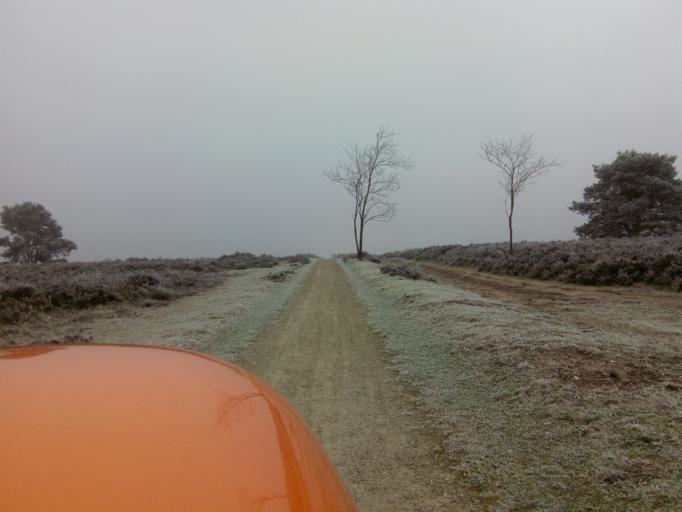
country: NL
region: Gelderland
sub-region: Gemeente Barneveld
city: Garderen
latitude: 52.2622
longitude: 5.7209
